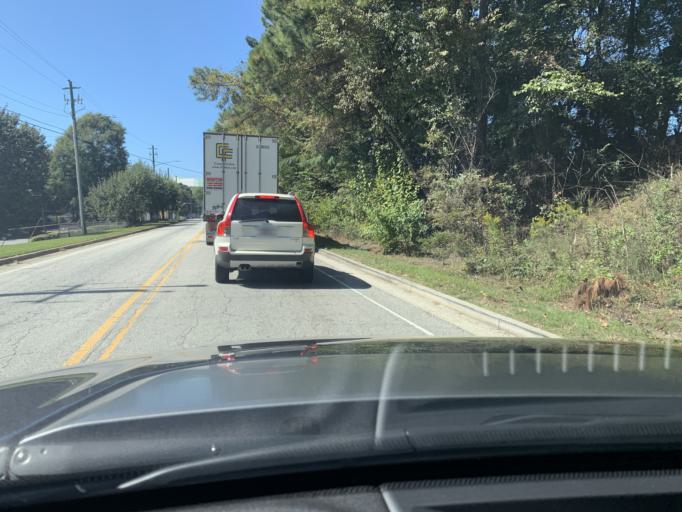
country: US
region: Georgia
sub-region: Clayton County
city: Conley
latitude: 33.6667
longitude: -84.3273
